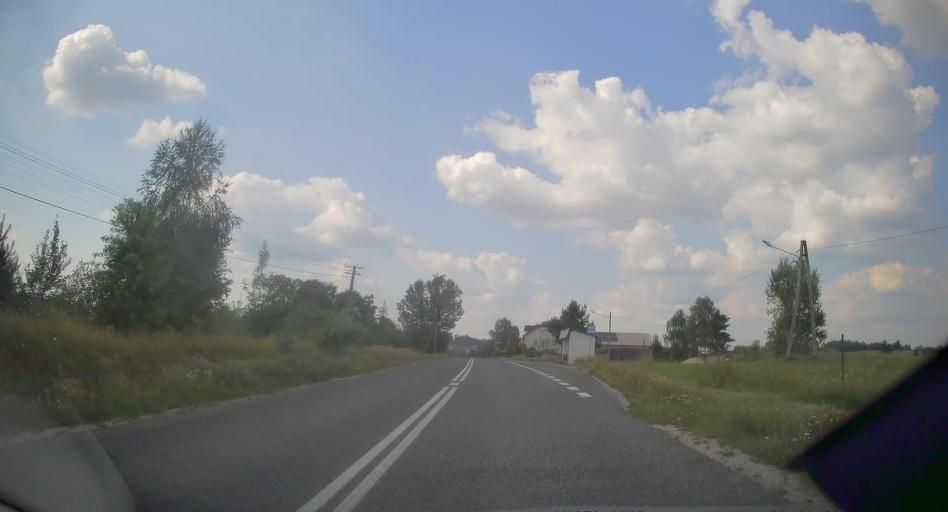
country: PL
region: Swietokrzyskie
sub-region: Powiat kielecki
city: Lopuszno
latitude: 50.9065
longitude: 20.2468
